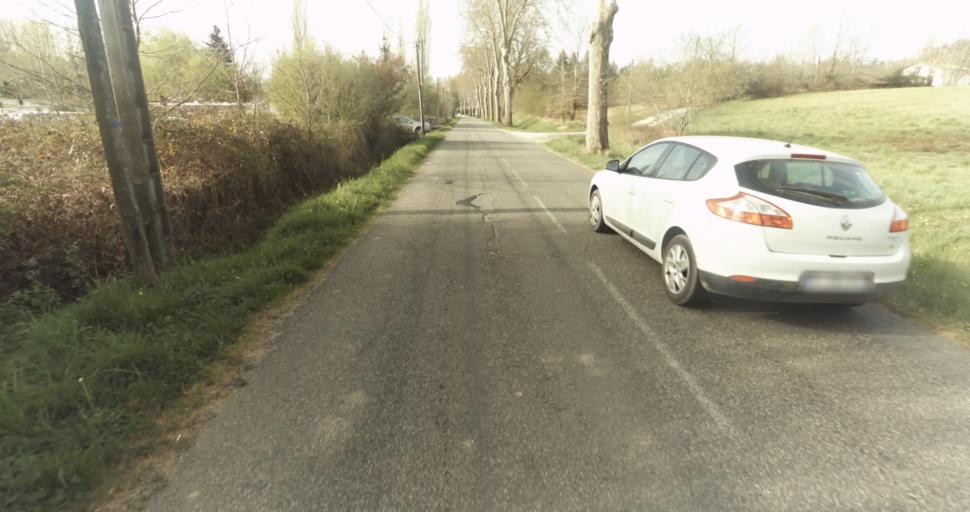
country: FR
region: Midi-Pyrenees
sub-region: Departement du Tarn-et-Garonne
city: Moissac
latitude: 44.1473
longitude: 1.1058
